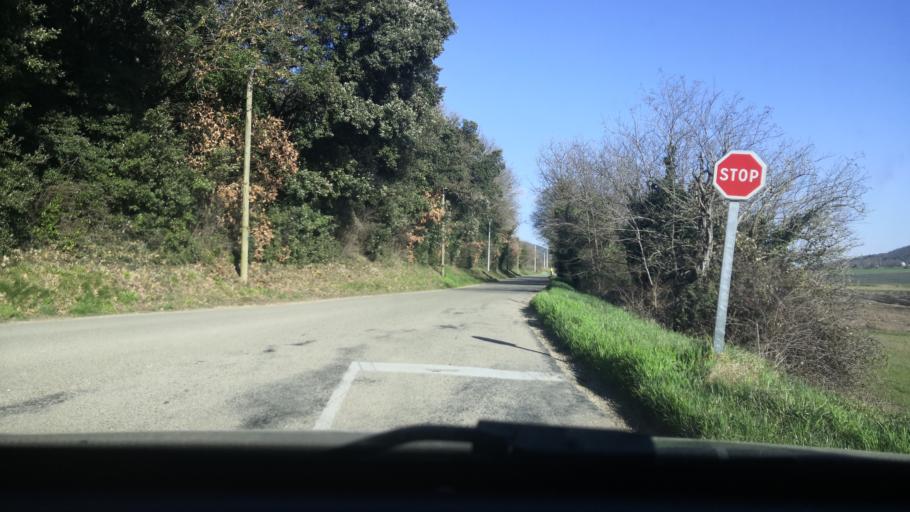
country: FR
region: Rhone-Alpes
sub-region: Departement de la Drome
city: Savasse
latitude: 44.6080
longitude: 4.7896
